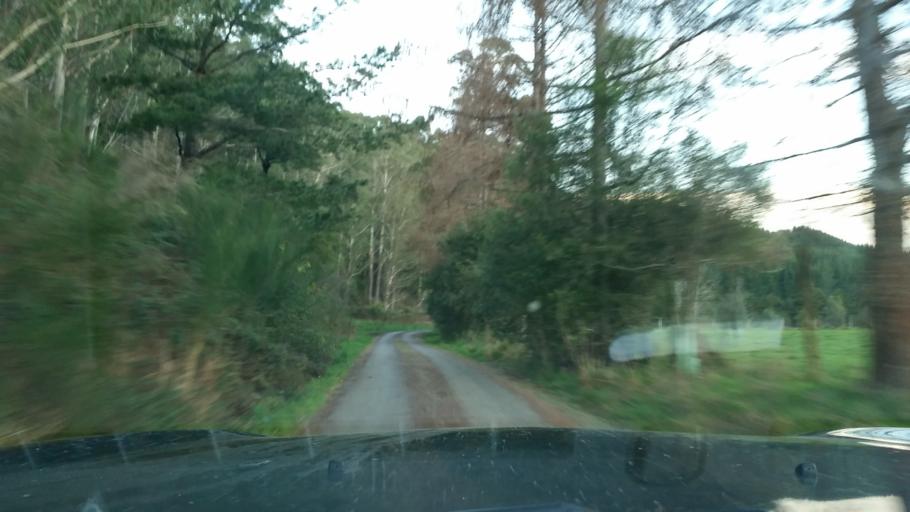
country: NZ
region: Marlborough
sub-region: Marlborough District
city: Blenheim
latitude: -41.4708
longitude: 173.7446
